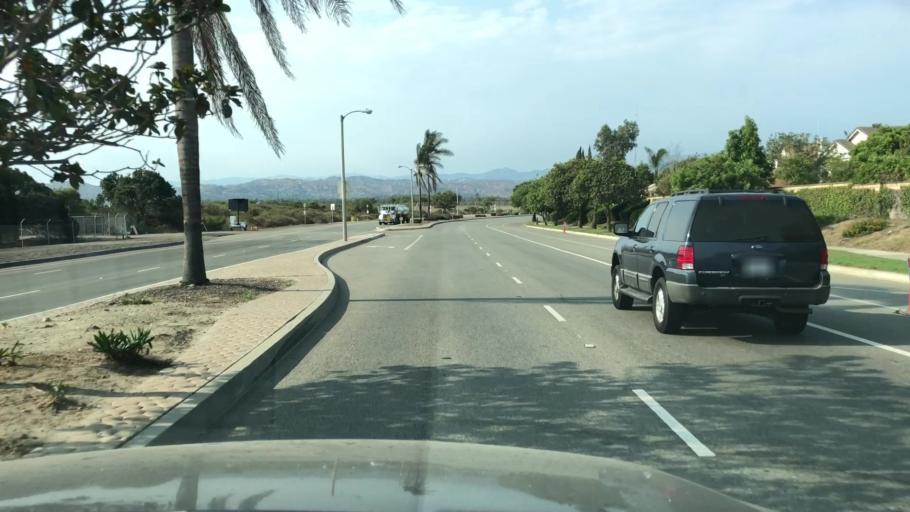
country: US
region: California
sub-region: Ventura County
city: El Rio
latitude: 34.2333
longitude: -119.1944
